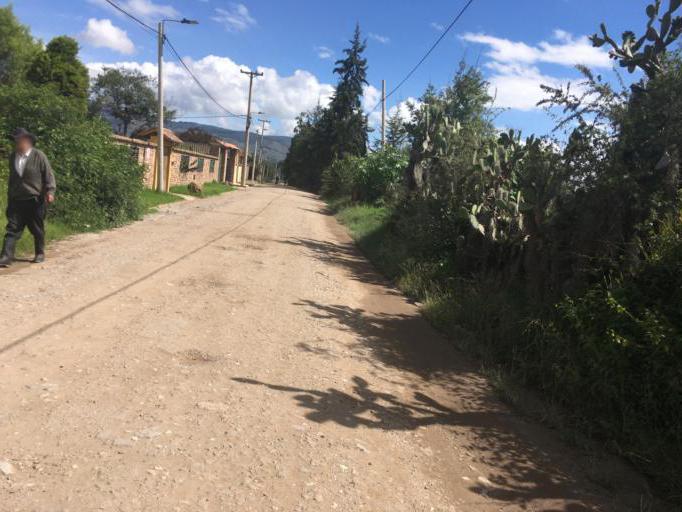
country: CO
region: Boyaca
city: Firavitoba
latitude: 5.6611
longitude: -72.9584
